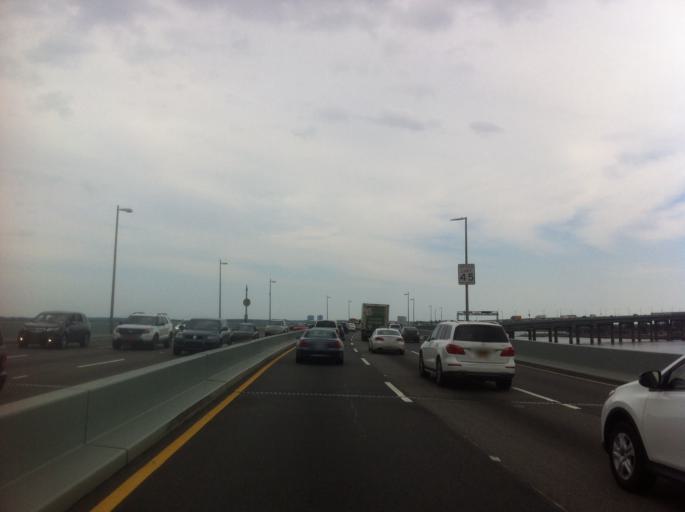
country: US
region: New York
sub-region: Nassau County
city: East Atlantic Beach
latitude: 40.8158
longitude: -73.7975
